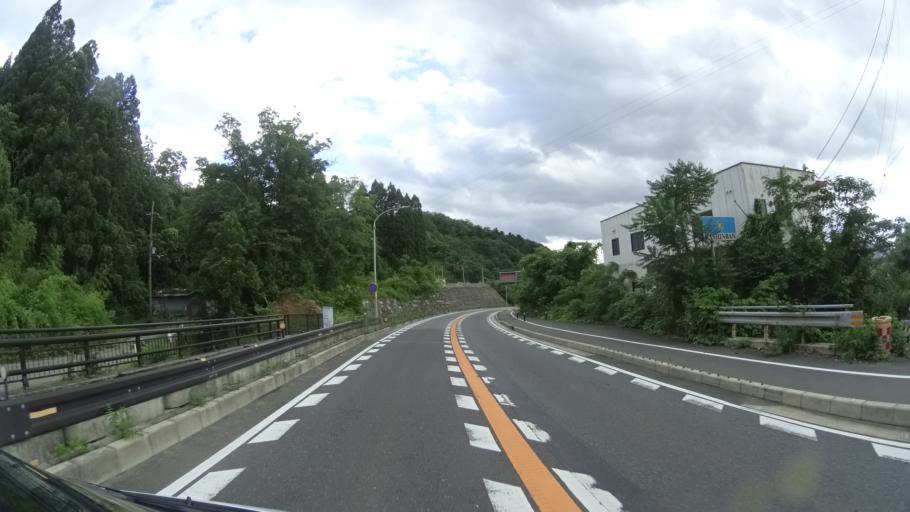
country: JP
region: Kyoto
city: Ayabe
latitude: 35.3061
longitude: 135.2749
